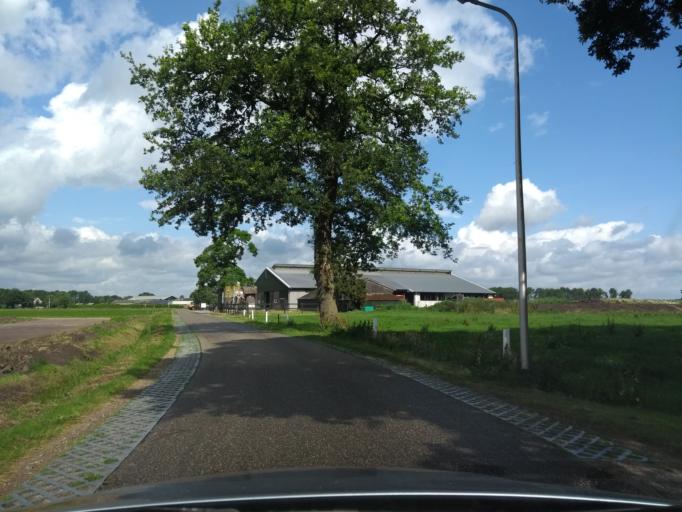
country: NL
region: Overijssel
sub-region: Gemeente Twenterand
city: Den Ham
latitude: 52.4316
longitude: 6.5106
